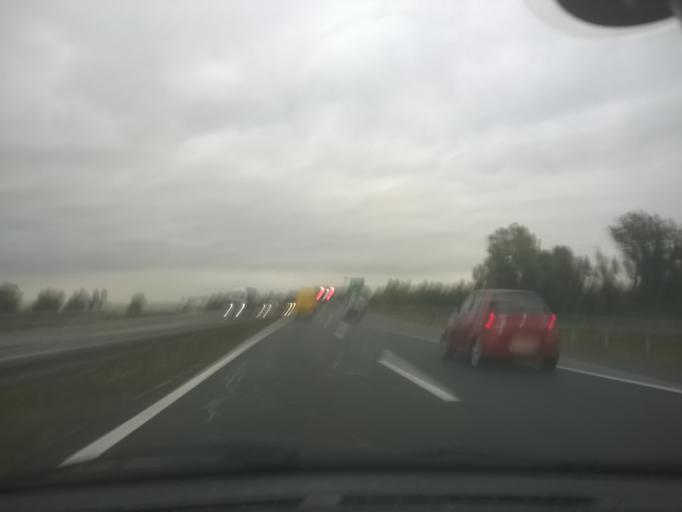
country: HR
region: Grad Zagreb
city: Jezdovec
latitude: 45.7979
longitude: 15.8431
